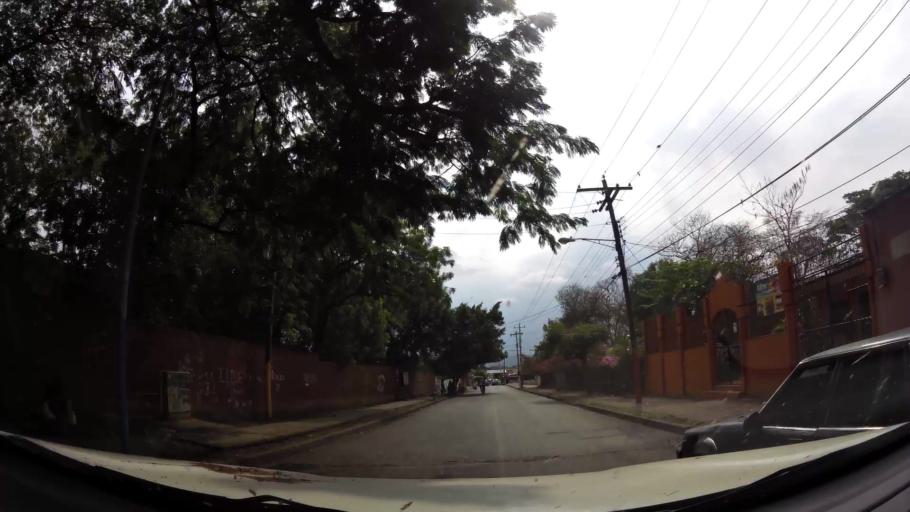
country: NI
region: Masaya
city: Masaya
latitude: 11.9756
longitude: -86.0888
